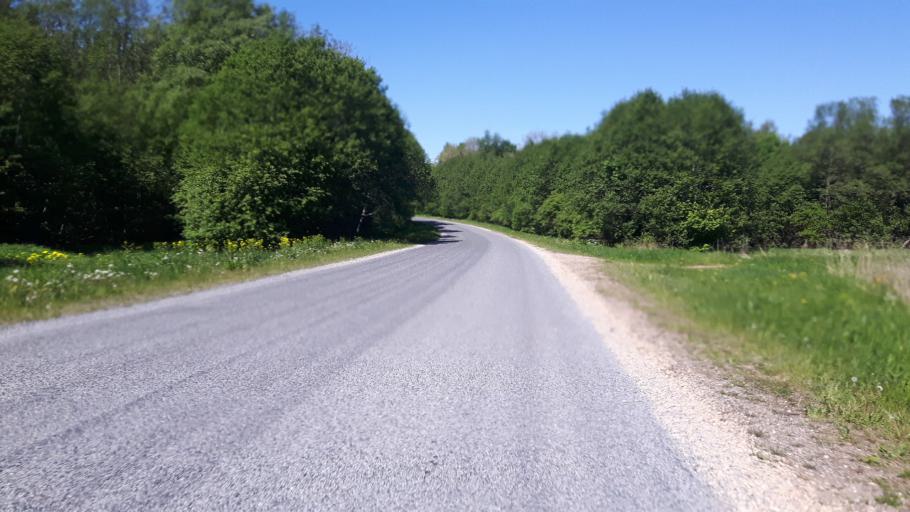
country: EE
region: Ida-Virumaa
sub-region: Sillamaee linn
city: Sillamae
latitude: 59.3761
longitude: 27.8388
